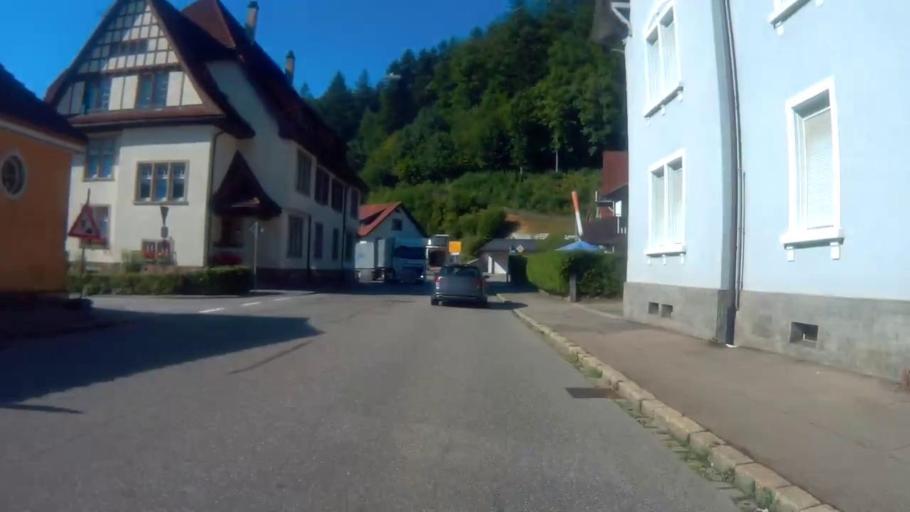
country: DE
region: Baden-Wuerttemberg
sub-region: Freiburg Region
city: Schonau im Schwarzwald
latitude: 47.7845
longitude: 7.8929
